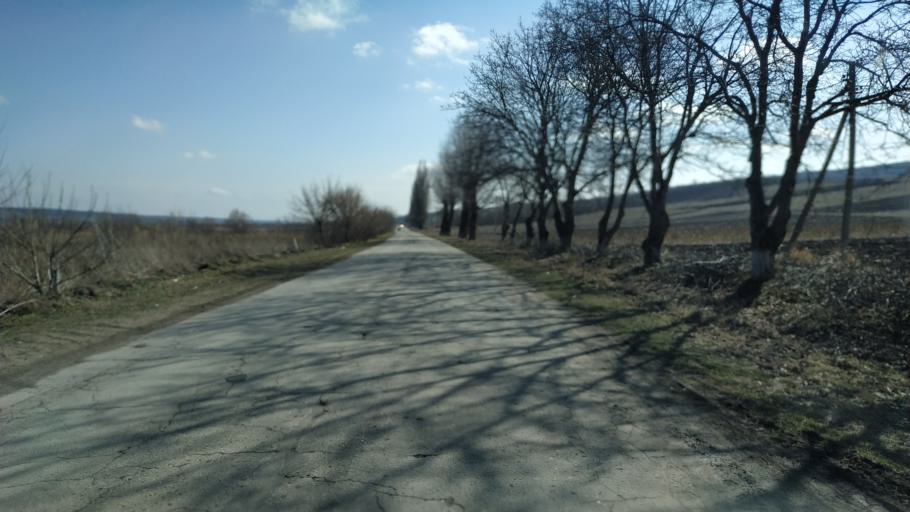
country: MD
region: Hincesti
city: Hincesti
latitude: 46.9482
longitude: 28.6168
